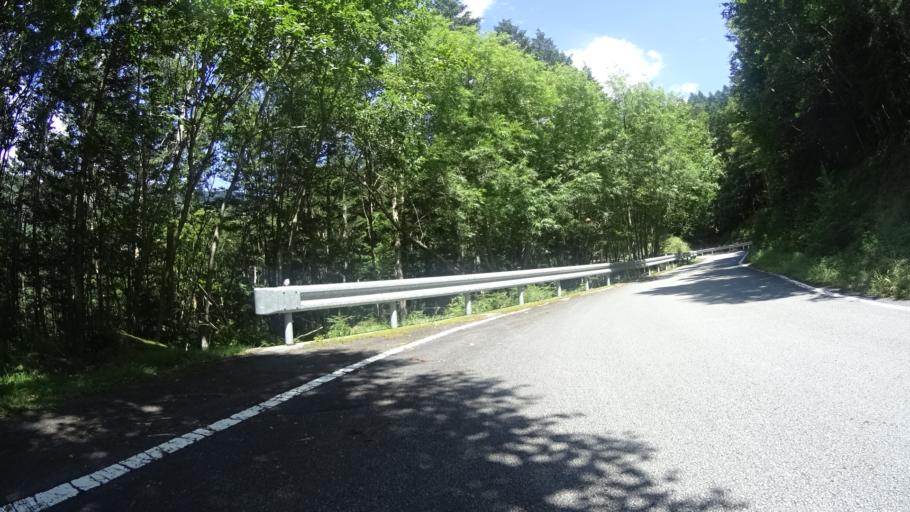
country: JP
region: Yamanashi
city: Enzan
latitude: 35.8566
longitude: 138.6449
